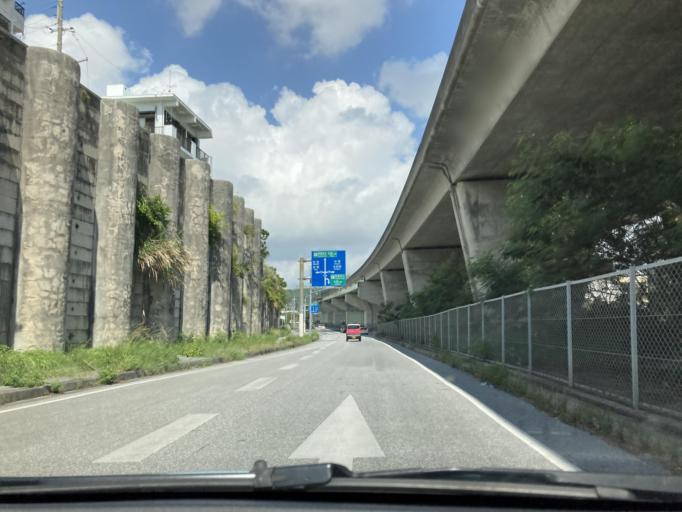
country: JP
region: Okinawa
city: Tomigusuku
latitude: 26.1985
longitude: 127.7397
